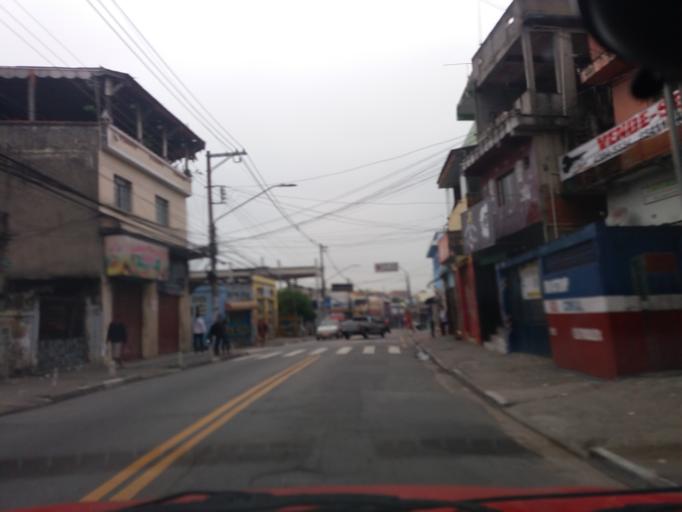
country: BR
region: Sao Paulo
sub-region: Osasco
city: Osasco
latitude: -23.5017
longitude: -46.7924
